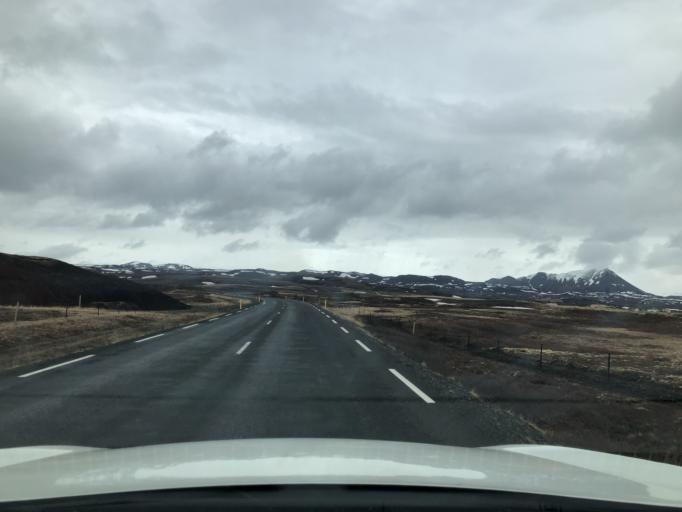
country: IS
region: Northeast
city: Laugar
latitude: 65.6486
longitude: -16.9964
